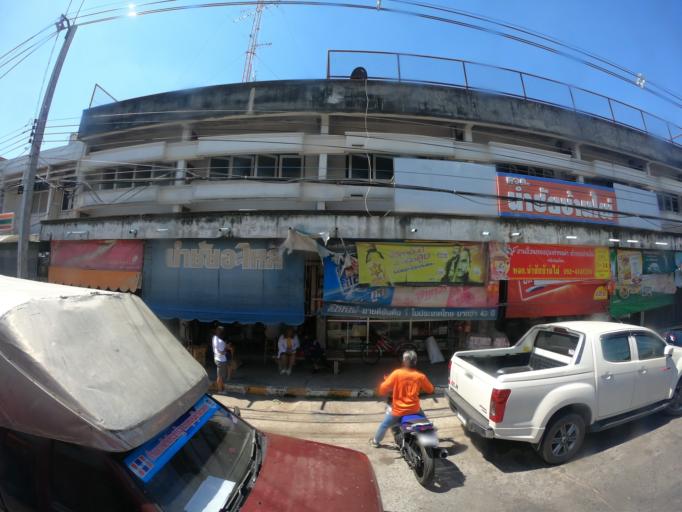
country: TH
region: Khon Kaen
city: Ban Phai
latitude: 16.0604
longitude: 102.7266
